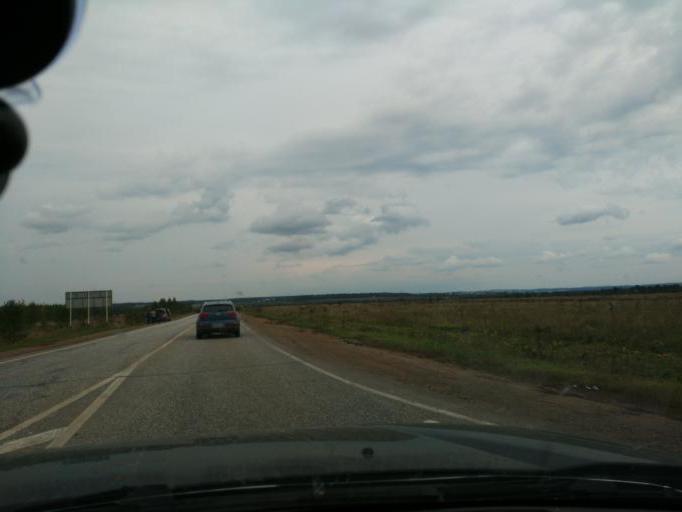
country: RU
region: Perm
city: Chernushka
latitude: 56.5046
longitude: 55.9898
